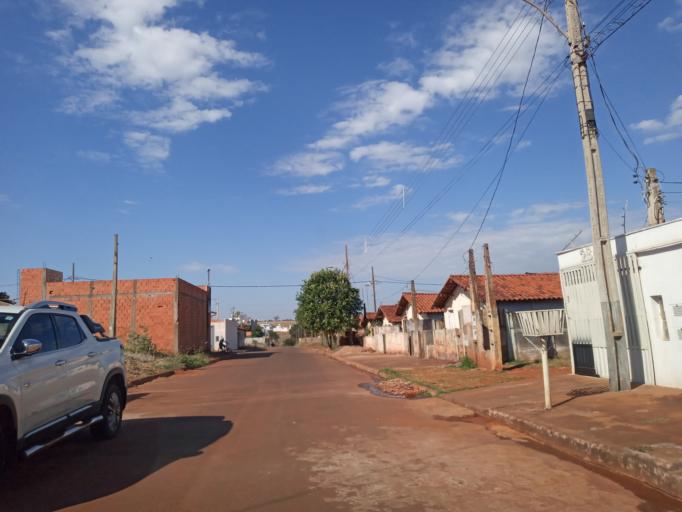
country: BR
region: Minas Gerais
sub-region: Ituiutaba
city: Ituiutaba
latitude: -18.9944
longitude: -49.4647
